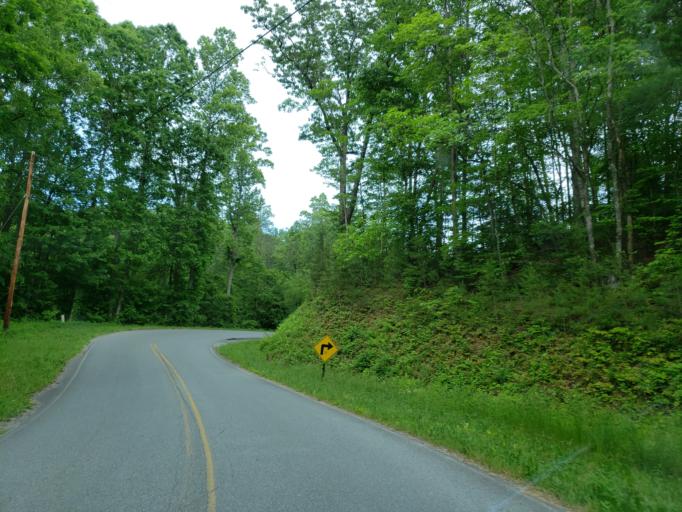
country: US
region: Georgia
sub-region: Fannin County
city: Blue Ridge
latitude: 34.8642
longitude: -84.3535
